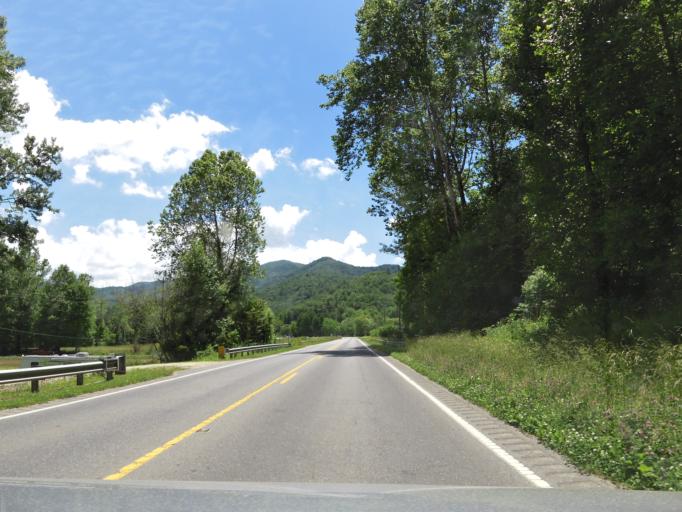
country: US
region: North Carolina
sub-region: Graham County
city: Robbinsville
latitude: 35.3058
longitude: -83.7949
